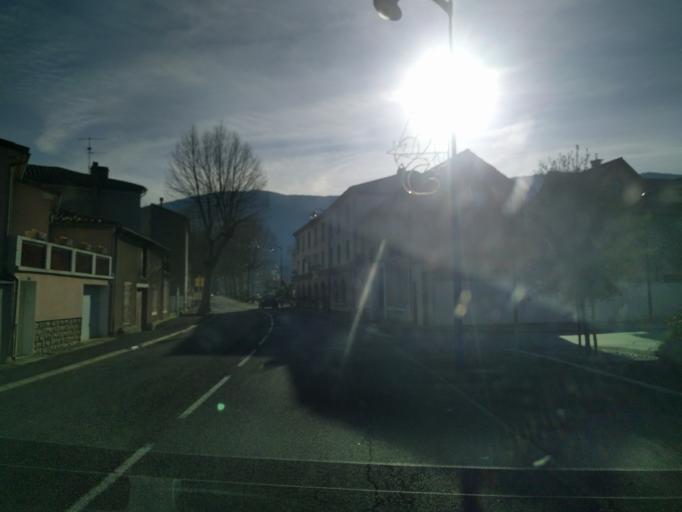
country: FR
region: Languedoc-Roussillon
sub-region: Departement de l'Aude
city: Quillan
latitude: 42.8762
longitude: 2.1823
